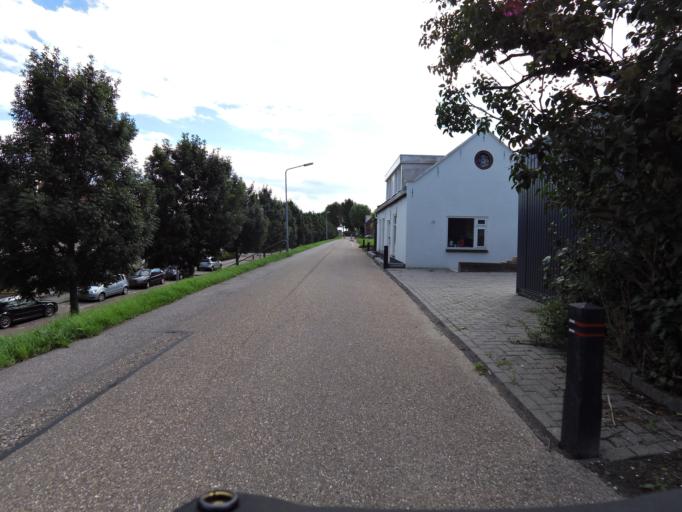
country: NL
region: North Brabant
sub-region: Gemeente Steenbergen
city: Dinteloord
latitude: 51.6866
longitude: 4.2805
